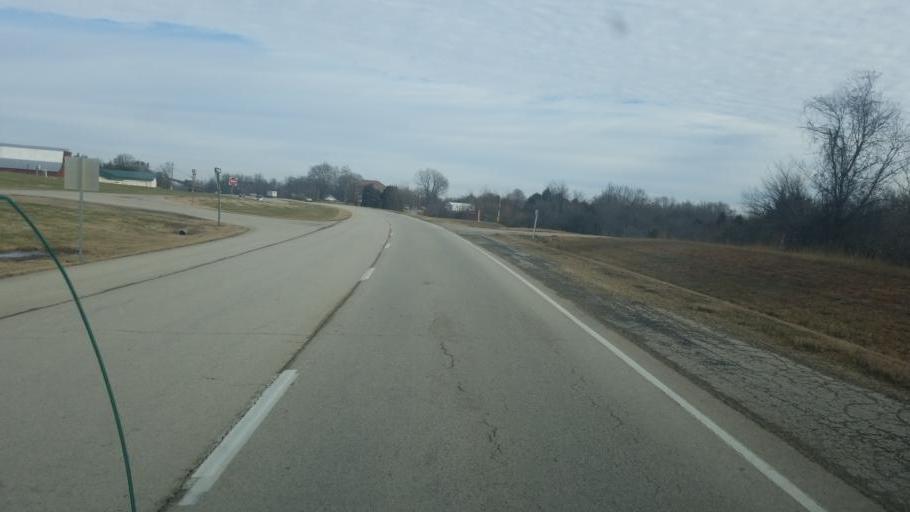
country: US
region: Missouri
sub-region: Stoddard County
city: Bloomfield
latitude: 36.8636
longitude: -89.9314
